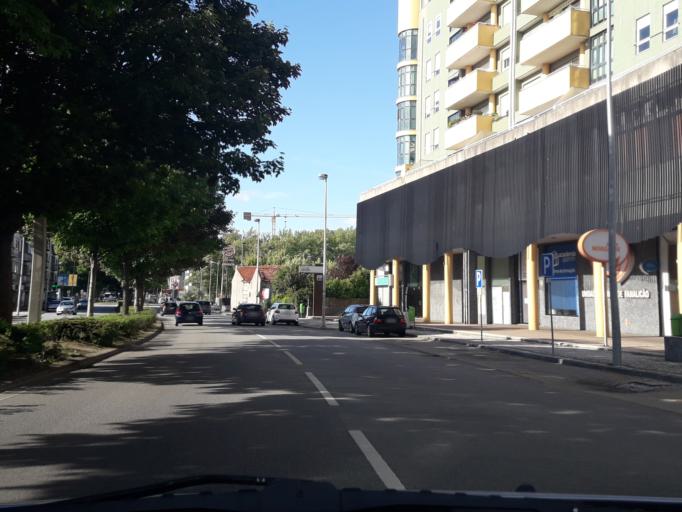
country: PT
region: Braga
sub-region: Vila Nova de Famalicao
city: Vila Nova de Famalicao
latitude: 41.4015
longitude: -8.5162
